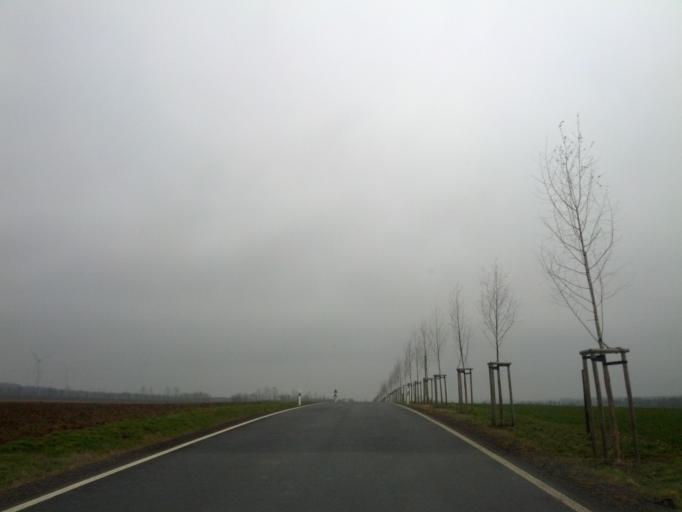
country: DE
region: Thuringia
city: Wangenheim
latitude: 51.0274
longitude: 10.6019
